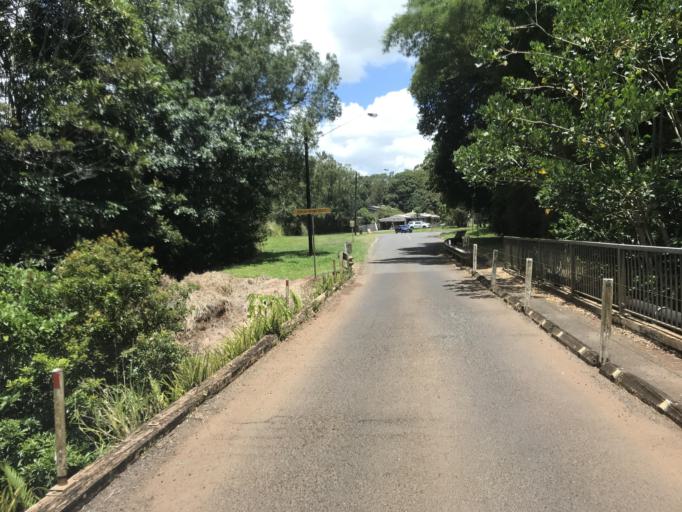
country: AU
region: Queensland
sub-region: Tablelands
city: Atherton
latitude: -17.3471
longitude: 145.5967
